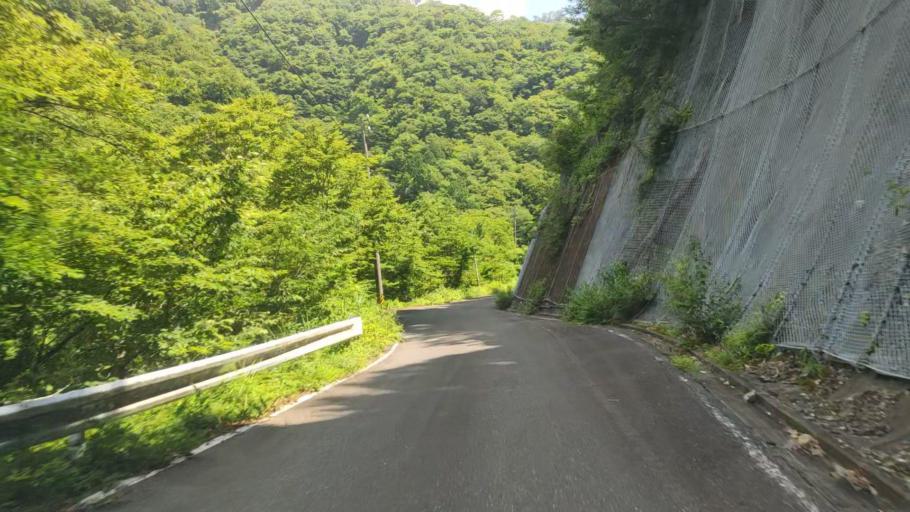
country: JP
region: Fukui
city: Ono
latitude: 35.7443
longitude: 136.5836
